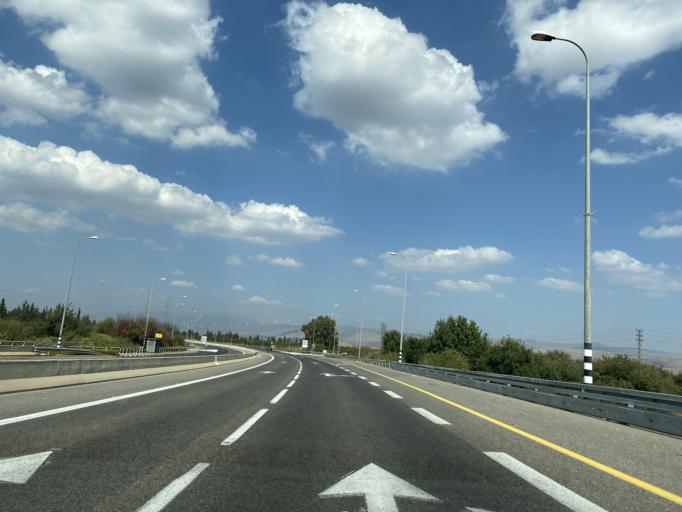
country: IL
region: Northern District
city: Rosh Pinna
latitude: 33.0306
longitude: 35.5706
